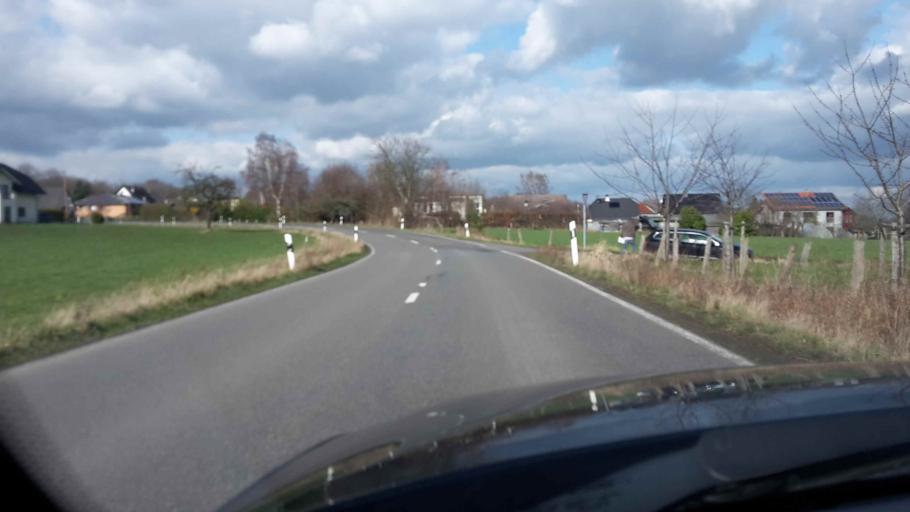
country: DE
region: North Rhine-Westphalia
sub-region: Regierungsbezirk Koln
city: Hennef
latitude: 50.7233
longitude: 7.3122
